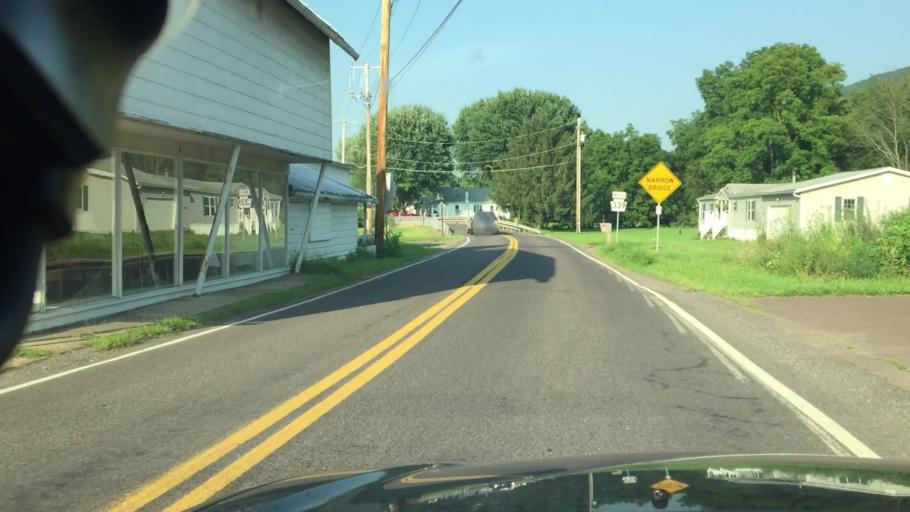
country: US
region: Pennsylvania
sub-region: Columbia County
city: Almedia
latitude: 40.9759
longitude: -76.3740
